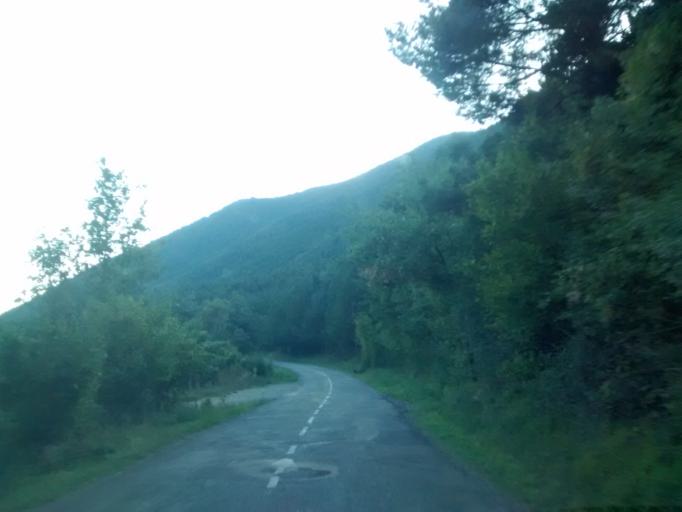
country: ES
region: Aragon
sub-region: Provincia de Huesca
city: Anso
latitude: 42.7805
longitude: -0.7409
